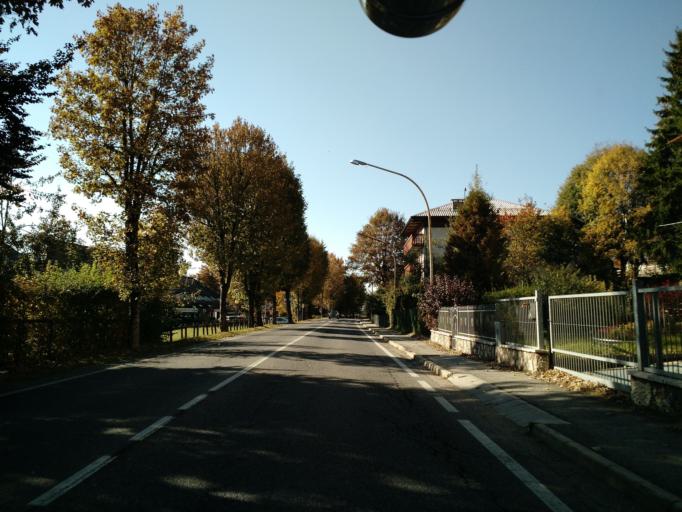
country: IT
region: Veneto
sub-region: Provincia di Vicenza
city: Gallio
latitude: 45.8874
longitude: 11.5401
